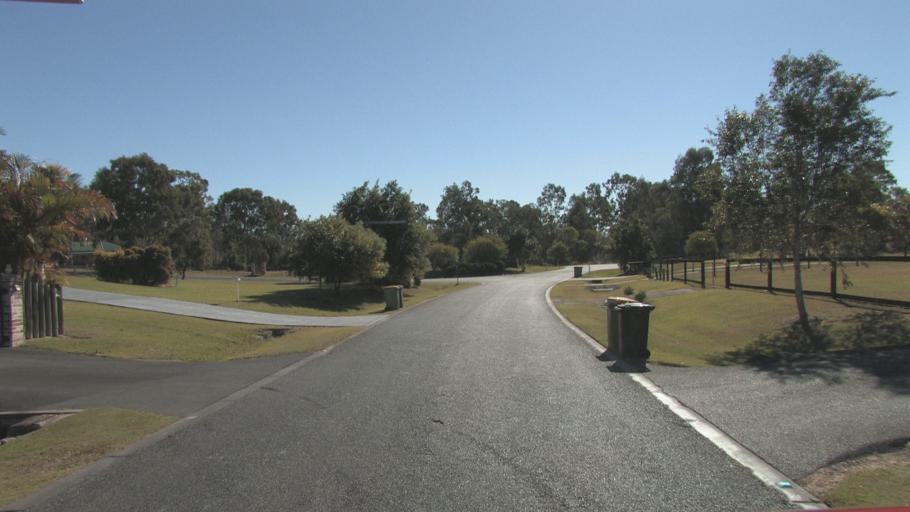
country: AU
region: Queensland
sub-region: Logan
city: North Maclean
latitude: -27.7452
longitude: 152.9461
